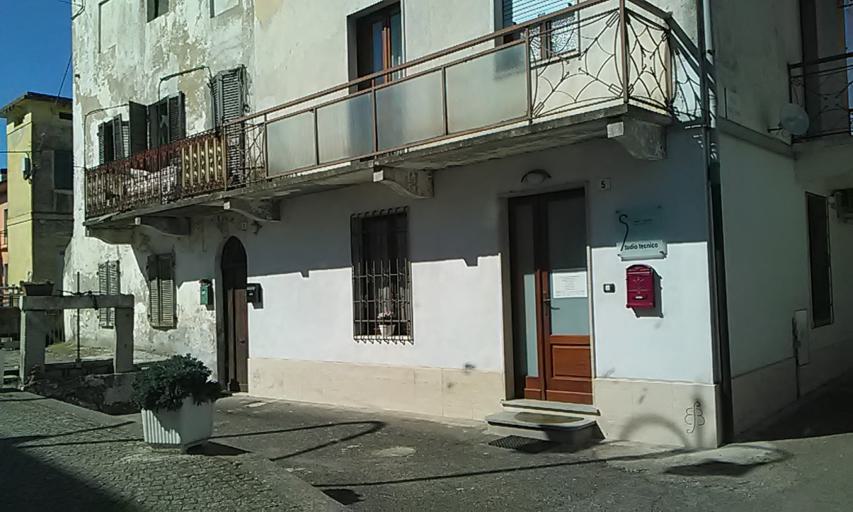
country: IT
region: Piedmont
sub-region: Provincia di Vercelli
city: Tricerro
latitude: 45.2335
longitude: 8.3244
